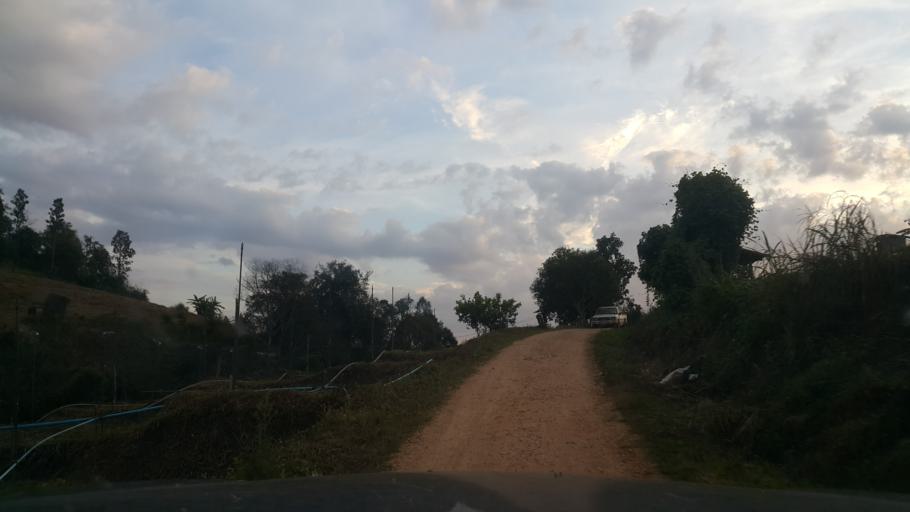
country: TH
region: Chiang Mai
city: Samoeng
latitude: 18.9630
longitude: 98.6776
